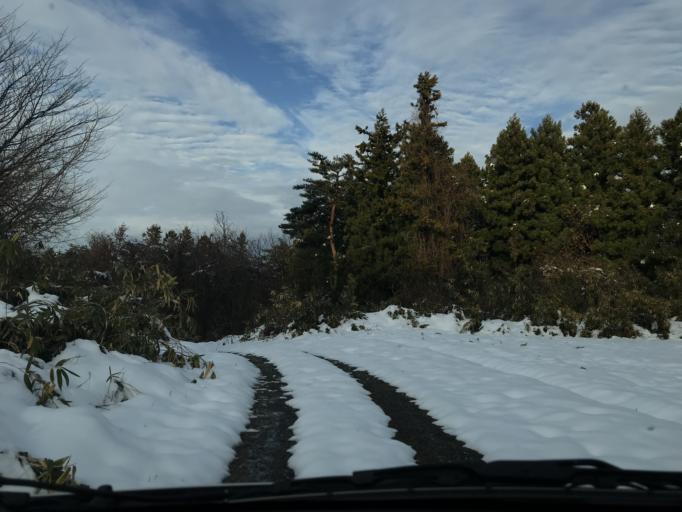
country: JP
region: Iwate
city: Mizusawa
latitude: 39.0367
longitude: 141.1044
